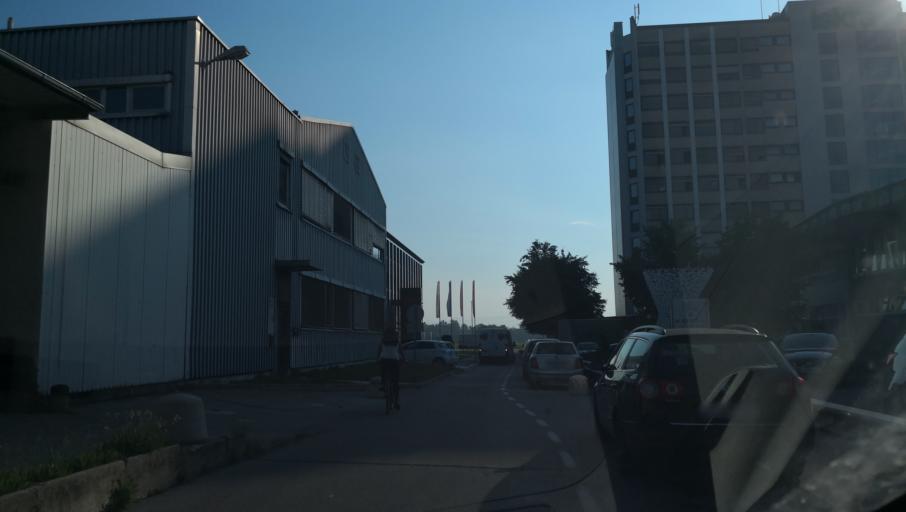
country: SI
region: Ljubljana
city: Ljubljana
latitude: 46.0863
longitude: 14.4821
